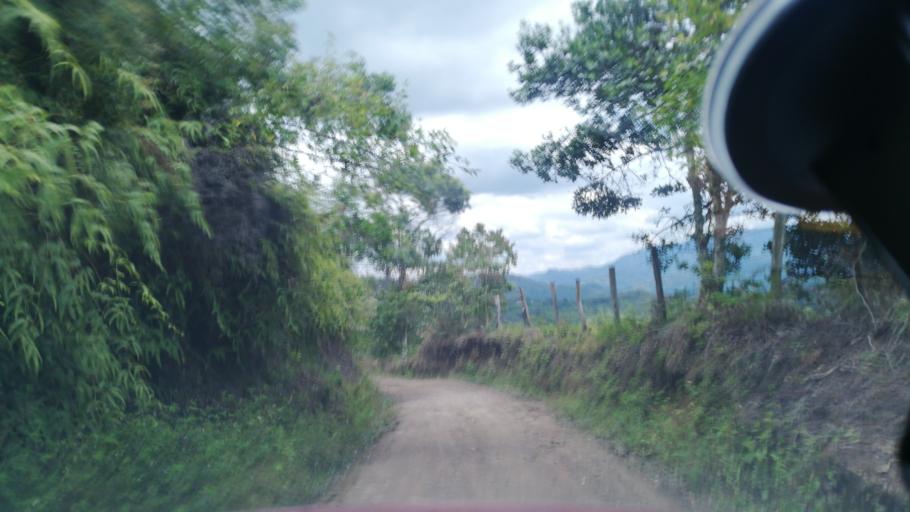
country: CO
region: Cundinamarca
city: Vergara
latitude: 5.1999
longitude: -74.2897
